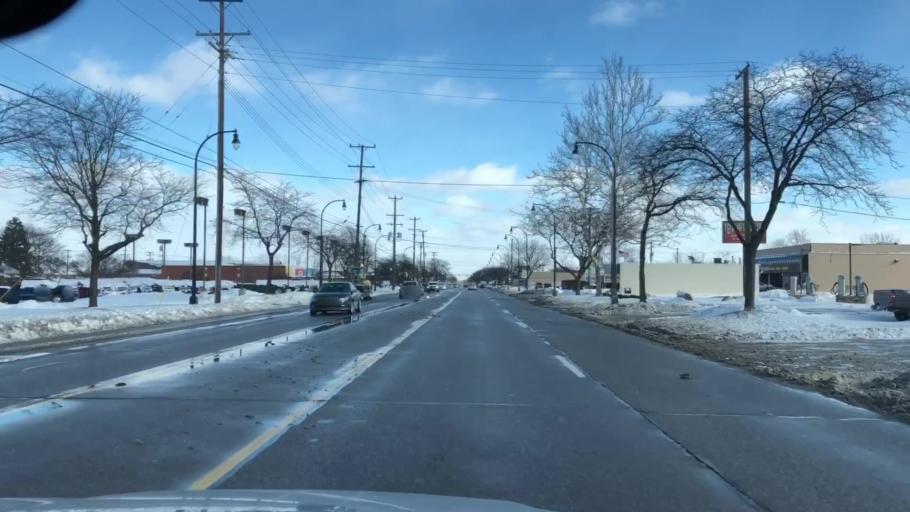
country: US
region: Michigan
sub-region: Wayne County
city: Livonia
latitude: 42.3682
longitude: -83.3775
